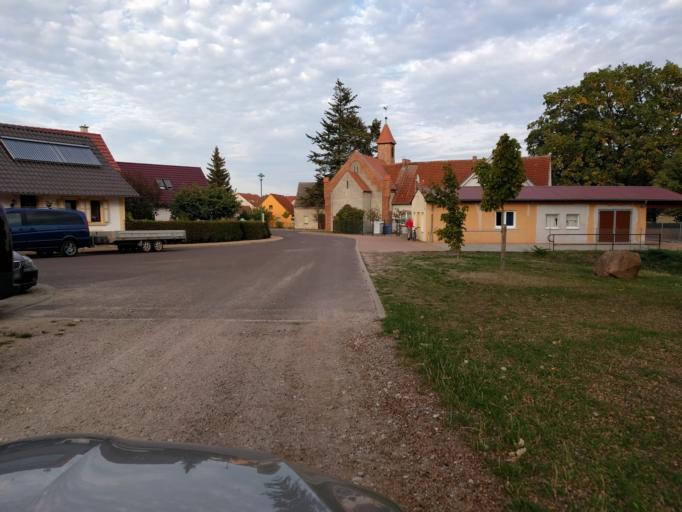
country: DE
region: Brandenburg
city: Ziesar
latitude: 52.2123
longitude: 12.2828
